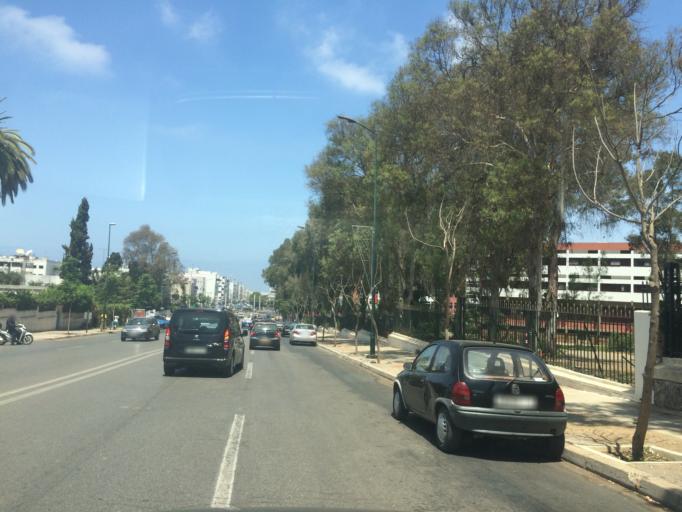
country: MA
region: Rabat-Sale-Zemmour-Zaer
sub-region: Rabat
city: Rabat
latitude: 33.9968
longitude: -6.8429
